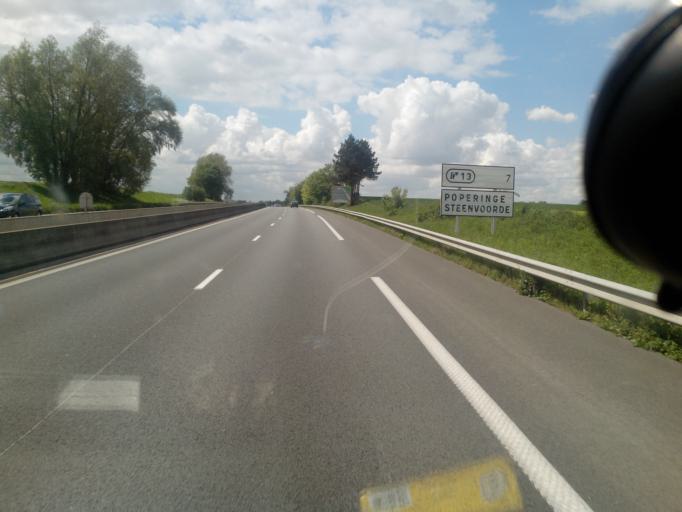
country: FR
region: Nord-Pas-de-Calais
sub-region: Departement du Nord
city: Meteren
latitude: 50.7509
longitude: 2.6655
